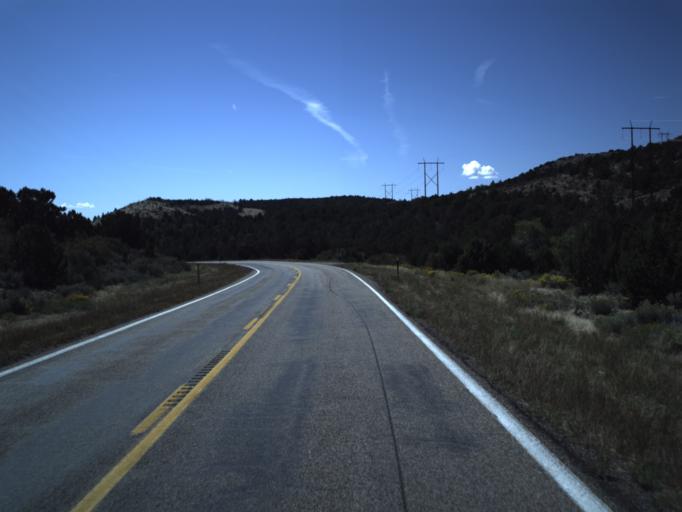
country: US
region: Utah
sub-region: Washington County
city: Enterprise
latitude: 37.4399
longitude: -113.6283
